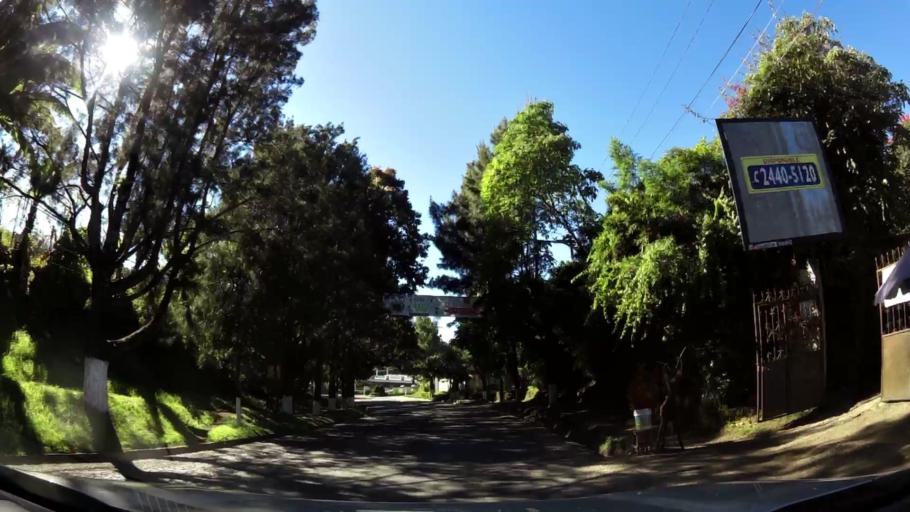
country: GT
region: Guatemala
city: Santa Catarina Pinula
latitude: 14.5246
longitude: -90.4667
